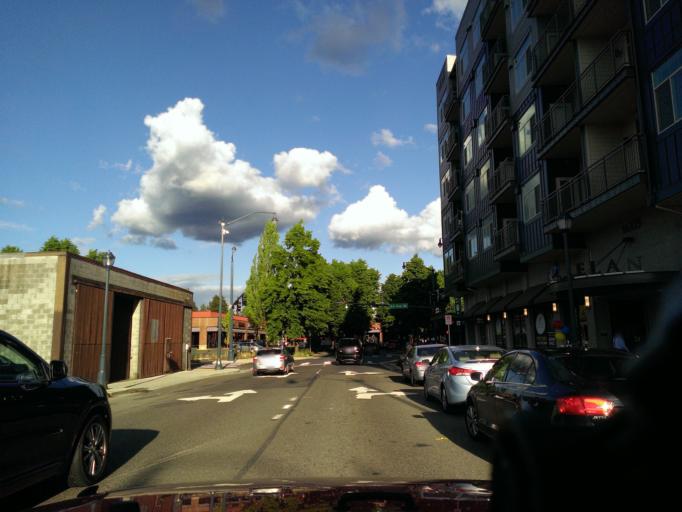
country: US
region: Washington
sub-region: King County
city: Redmond
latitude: 47.6732
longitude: -122.1223
